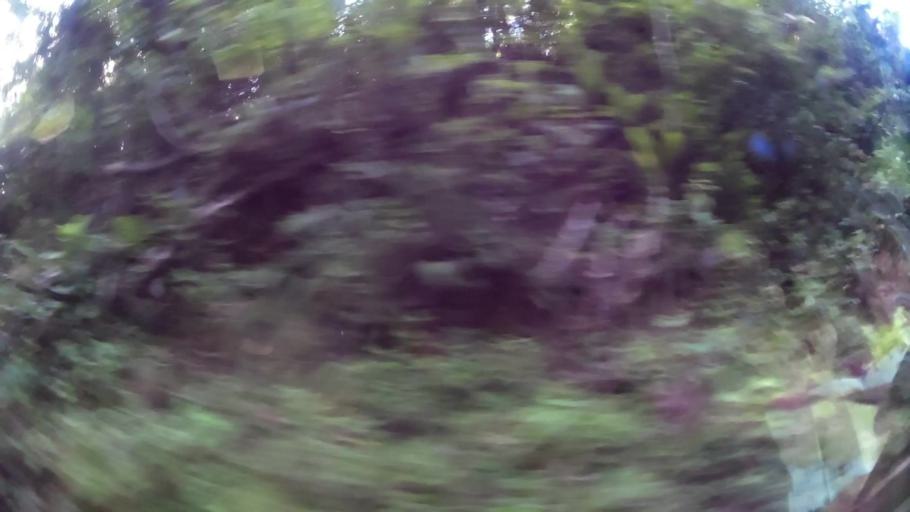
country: DM
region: Saint John
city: Portsmouth
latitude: 15.5735
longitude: -61.4308
